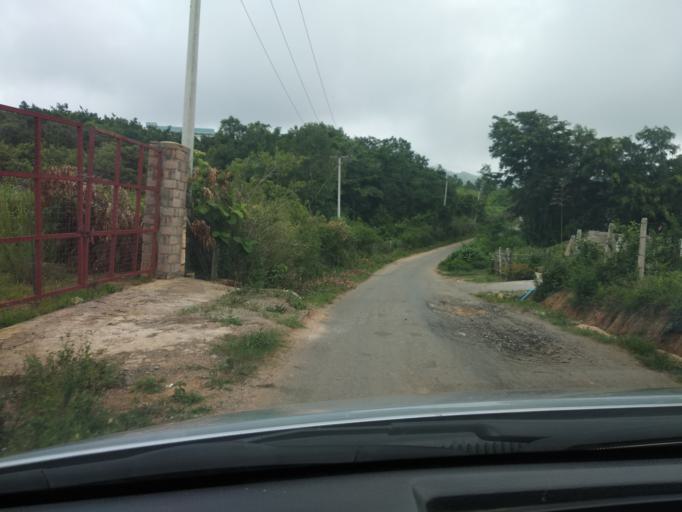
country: MM
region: Mandalay
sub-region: Pyin Oo Lwin District
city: Pyin Oo Lwin
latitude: 21.9176
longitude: 96.3835
